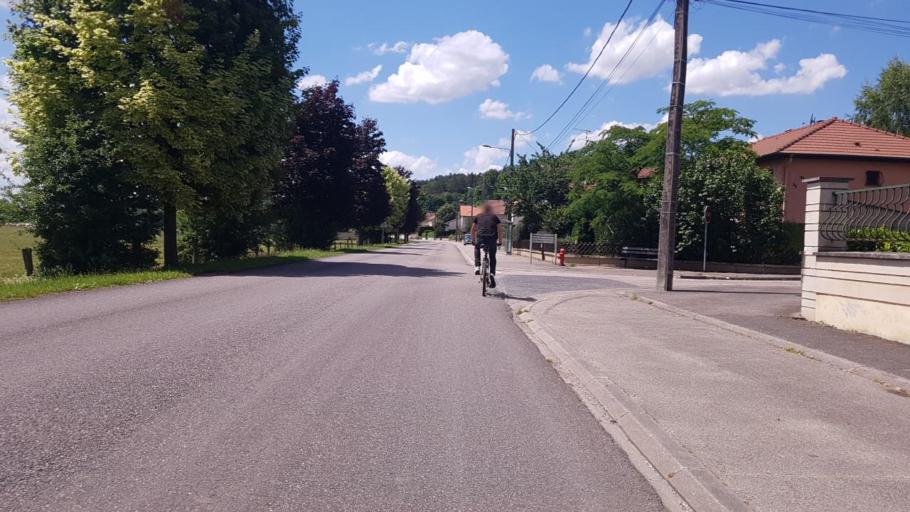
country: FR
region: Lorraine
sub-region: Departement de la Meuse
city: Vacon
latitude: 48.6840
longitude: 5.6143
